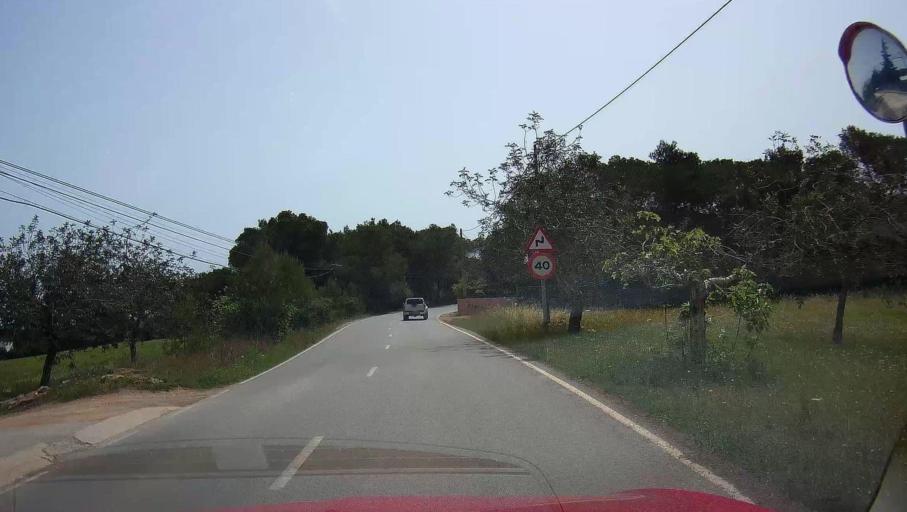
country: ES
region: Balearic Islands
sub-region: Illes Balears
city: Santa Eularia des Riu
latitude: 39.0082
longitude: 1.5695
